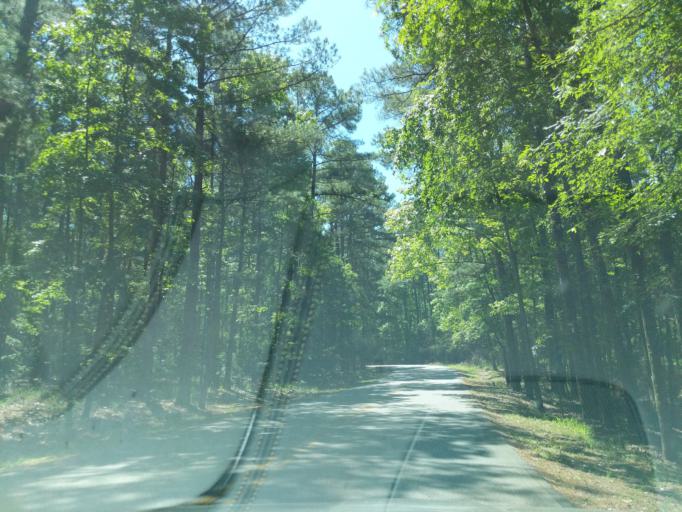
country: US
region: Georgia
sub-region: Columbia County
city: Appling
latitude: 33.6647
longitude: -82.3846
